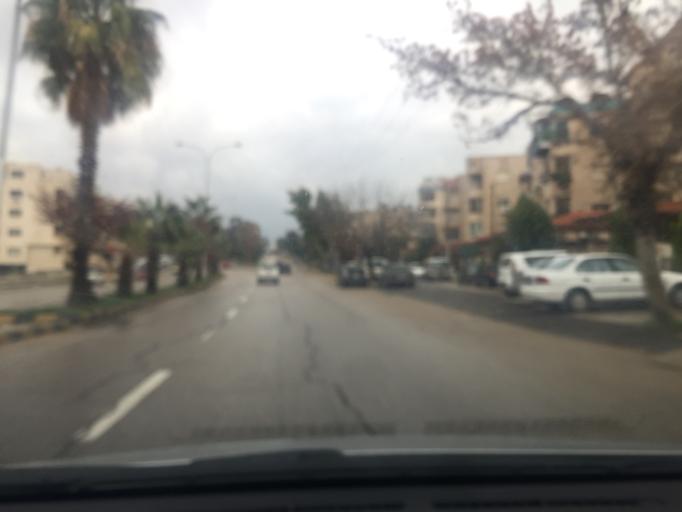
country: JO
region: Amman
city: Amman
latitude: 31.9786
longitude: 35.9331
